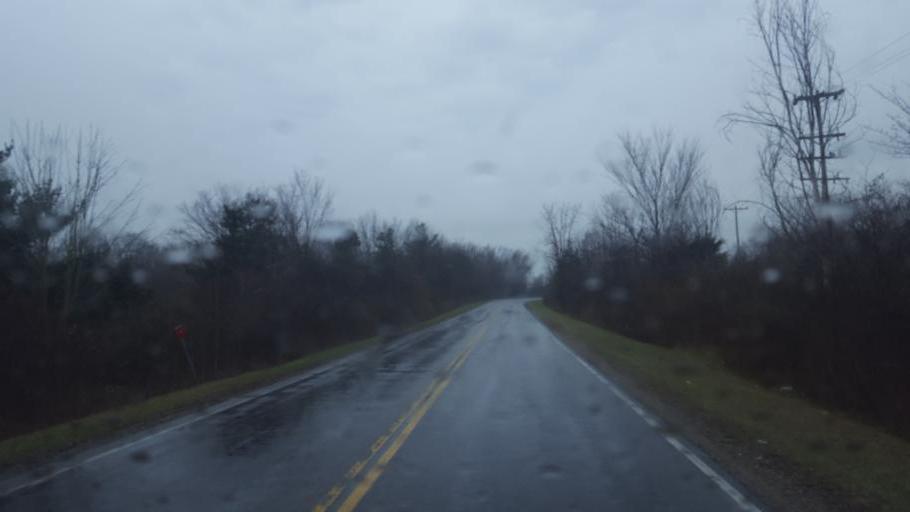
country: US
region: Ohio
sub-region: Delaware County
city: Lewis Center
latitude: 40.2395
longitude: -82.9830
